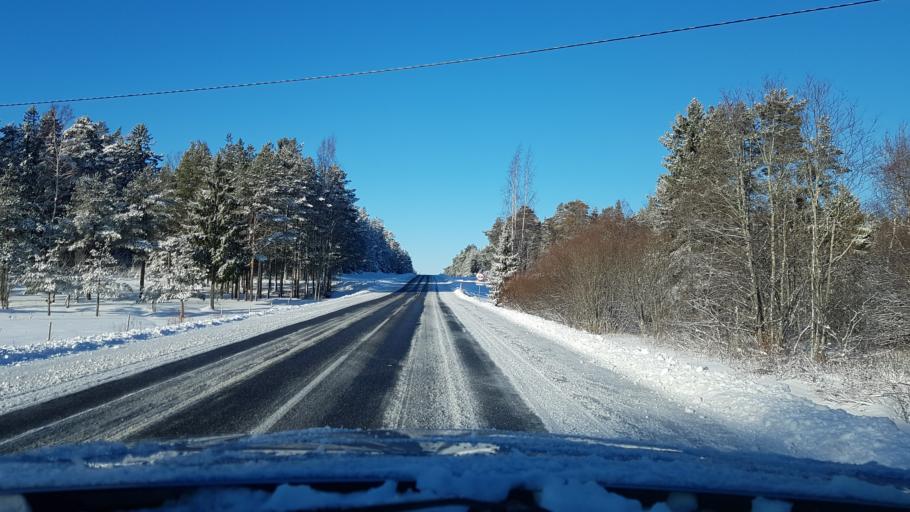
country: EE
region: Hiiumaa
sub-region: Kaerdla linn
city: Kardla
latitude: 58.9583
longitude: 22.8580
